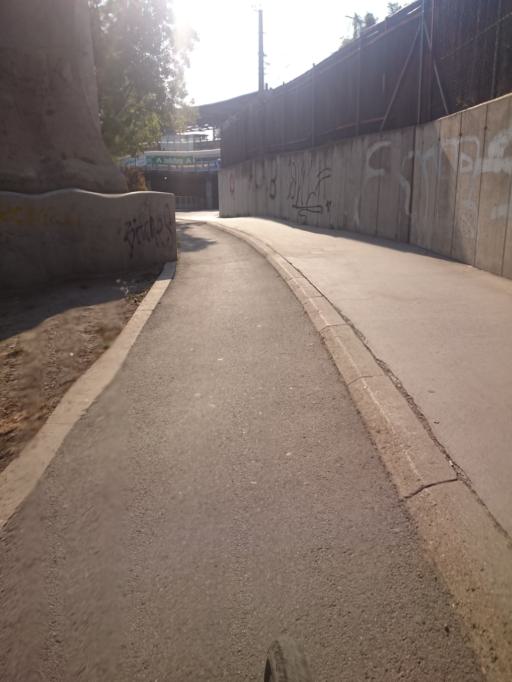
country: AT
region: Lower Austria
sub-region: Politischer Bezirk Wien-Umgebung
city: Gerasdorf bei Wien
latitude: 48.2711
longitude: 16.4197
